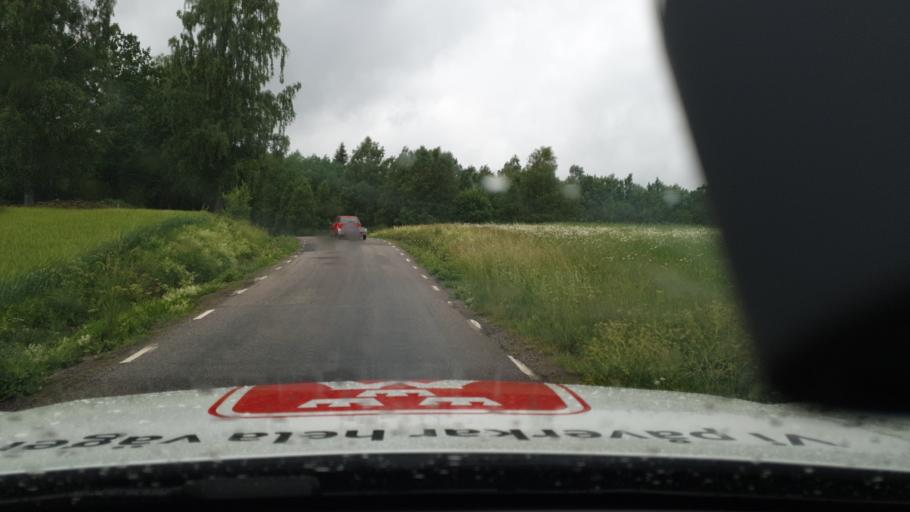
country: SE
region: Joenkoeping
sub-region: Mullsjo Kommun
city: Mullsjoe
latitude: 57.9608
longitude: 13.6693
